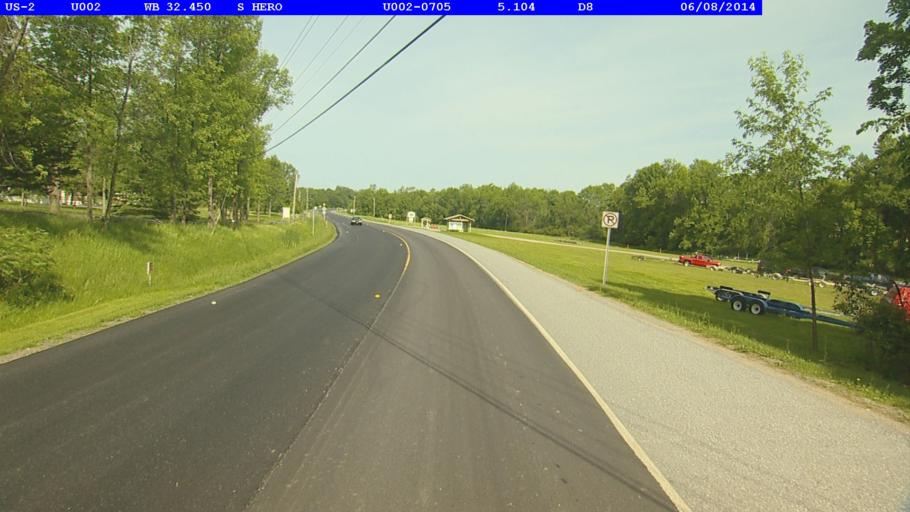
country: US
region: Vermont
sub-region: Chittenden County
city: Colchester
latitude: 44.6366
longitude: -73.2677
